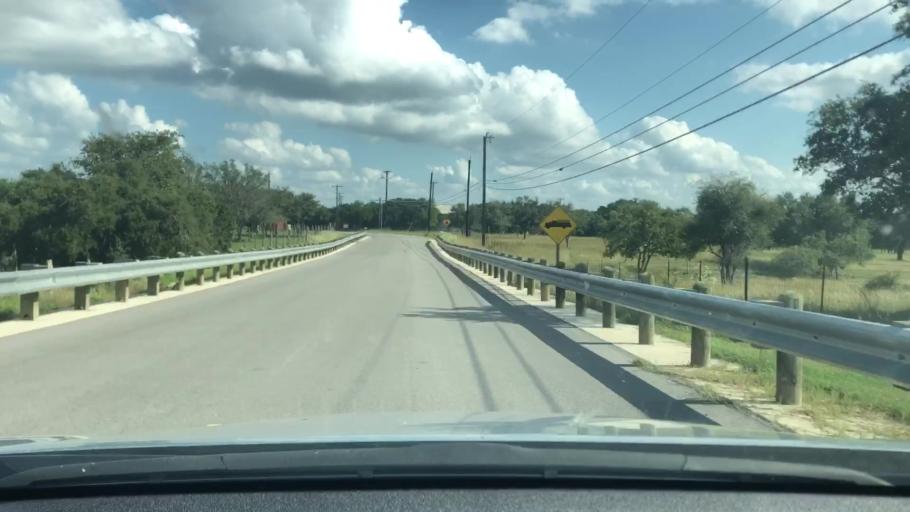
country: US
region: Texas
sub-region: Bexar County
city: Fair Oaks Ranch
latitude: 29.7565
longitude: -98.6249
